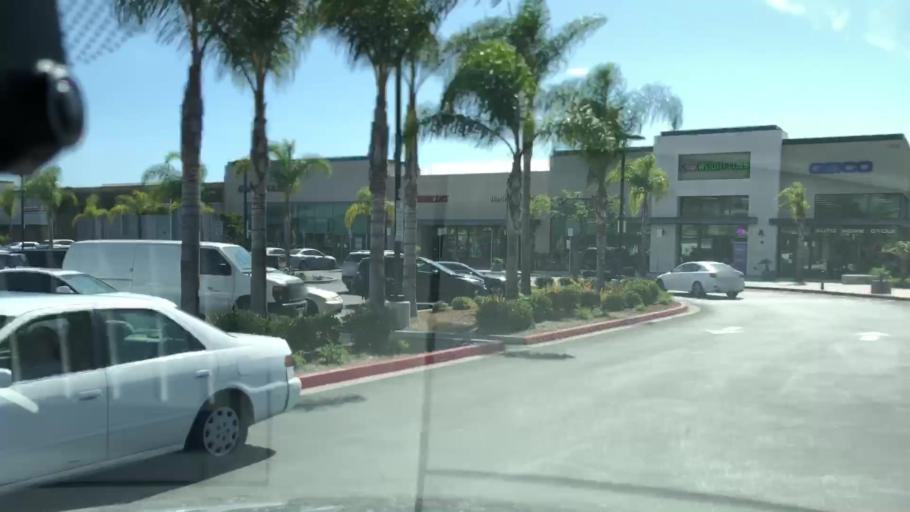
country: US
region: California
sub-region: Ventura County
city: El Rio
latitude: 34.2183
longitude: -119.1606
